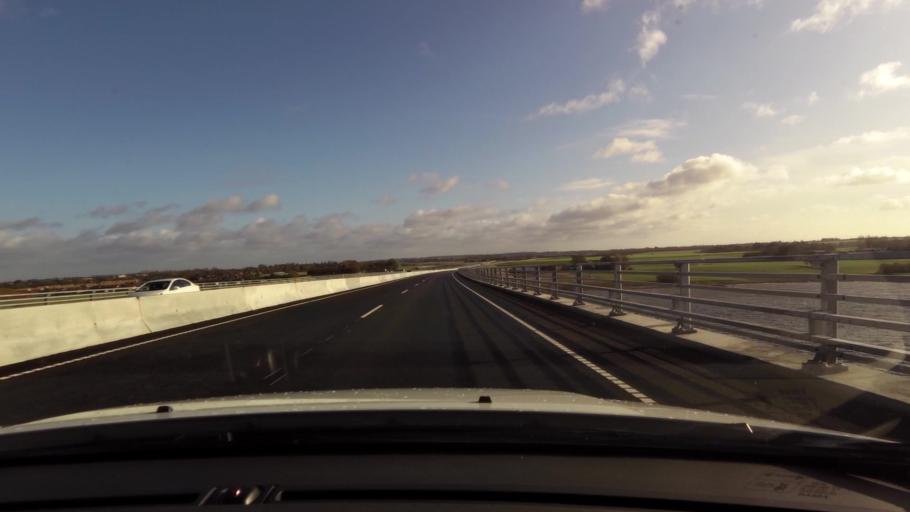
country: DK
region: Capital Region
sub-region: Frederikssund Kommune
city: Frederikssund
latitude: 55.8129
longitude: 12.0628
